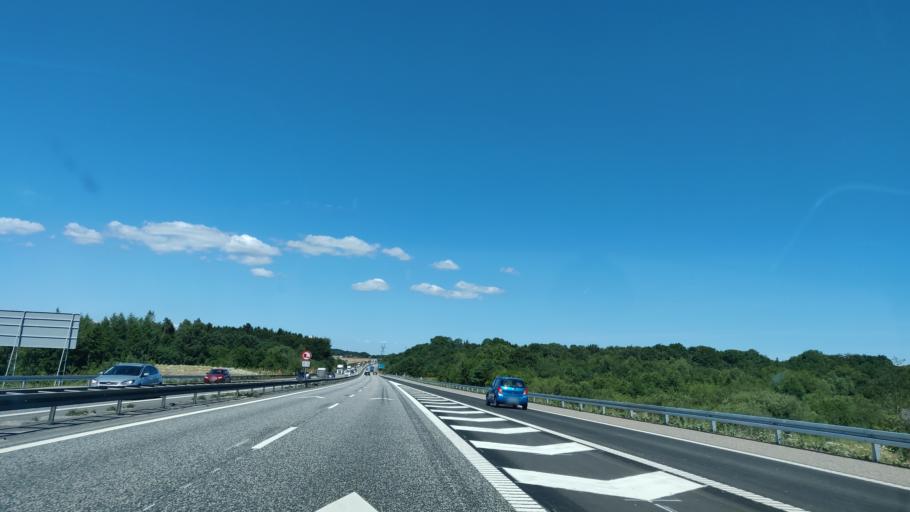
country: DK
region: Central Jutland
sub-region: Horsens Kommune
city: Horsens
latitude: 55.8702
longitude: 9.7708
